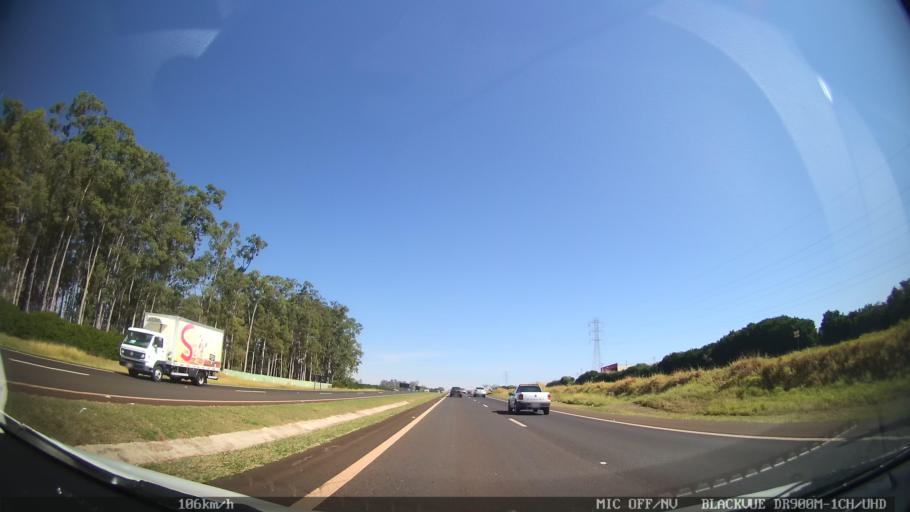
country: BR
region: Sao Paulo
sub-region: Ribeirao Preto
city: Ribeirao Preto
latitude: -21.1222
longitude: -47.8366
